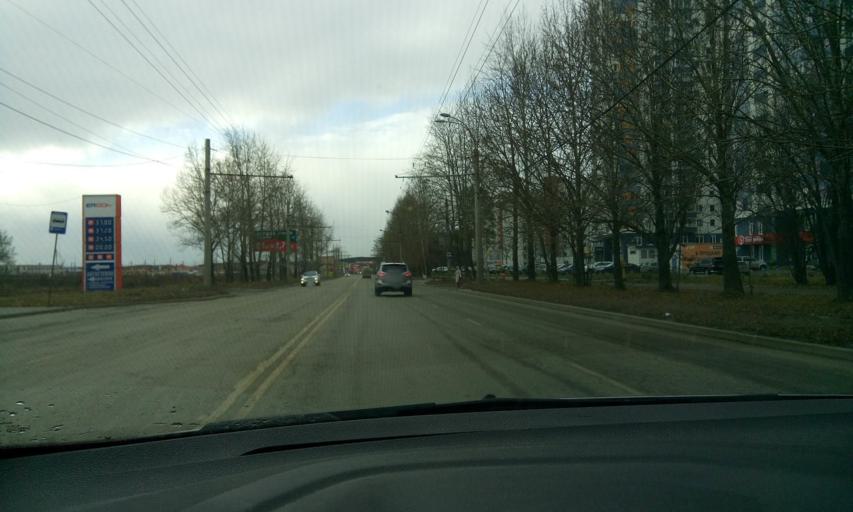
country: RU
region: Sverdlovsk
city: Sovkhoznyy
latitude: 56.7734
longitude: 60.5469
